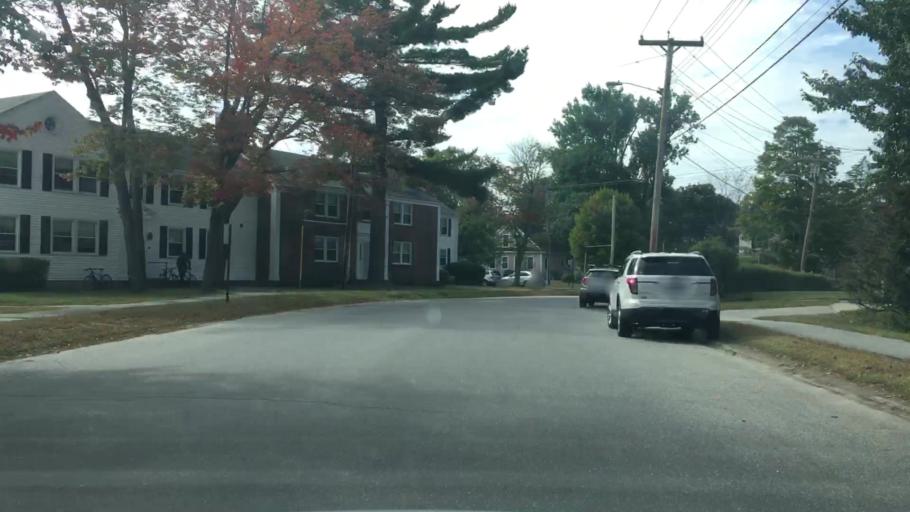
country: US
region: Maine
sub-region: Cumberland County
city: Brunswick
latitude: 43.9041
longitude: -69.9652
